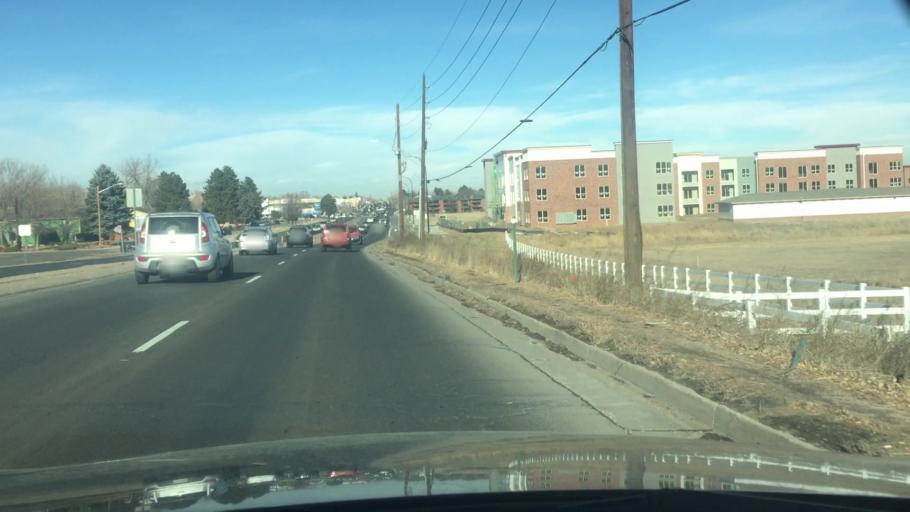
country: US
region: Colorado
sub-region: Jefferson County
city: Lakewood
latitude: 39.6753
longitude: -105.0813
